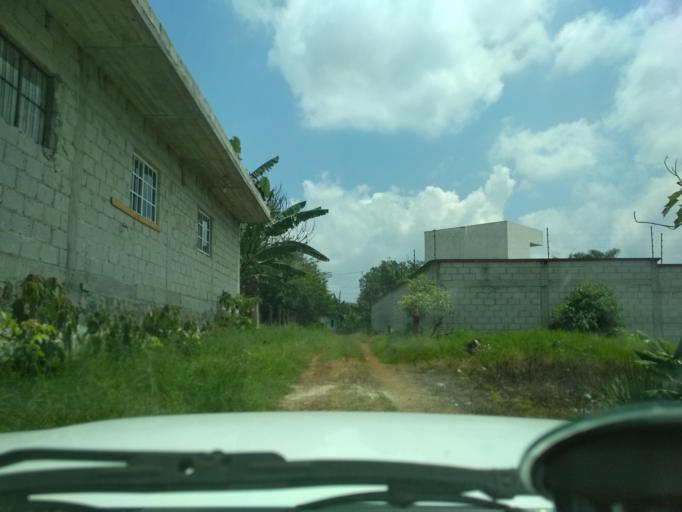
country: MX
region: Veracruz
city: Monte Blanco
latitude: 18.9676
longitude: -97.0120
